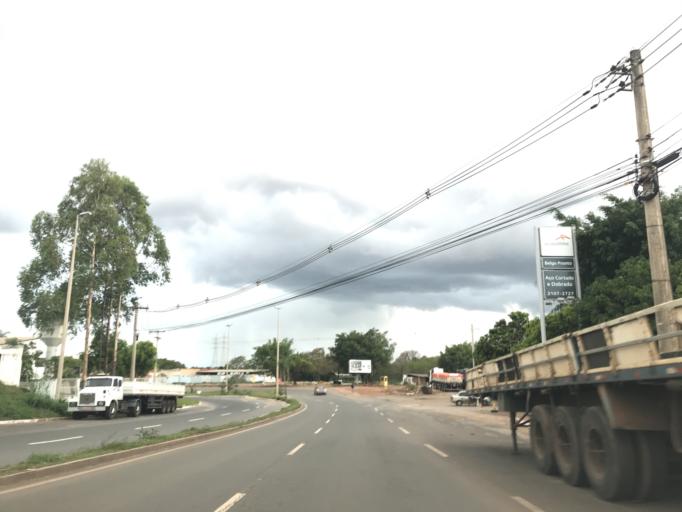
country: BR
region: Federal District
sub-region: Brasilia
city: Brasilia
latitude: -15.8031
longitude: -47.9714
